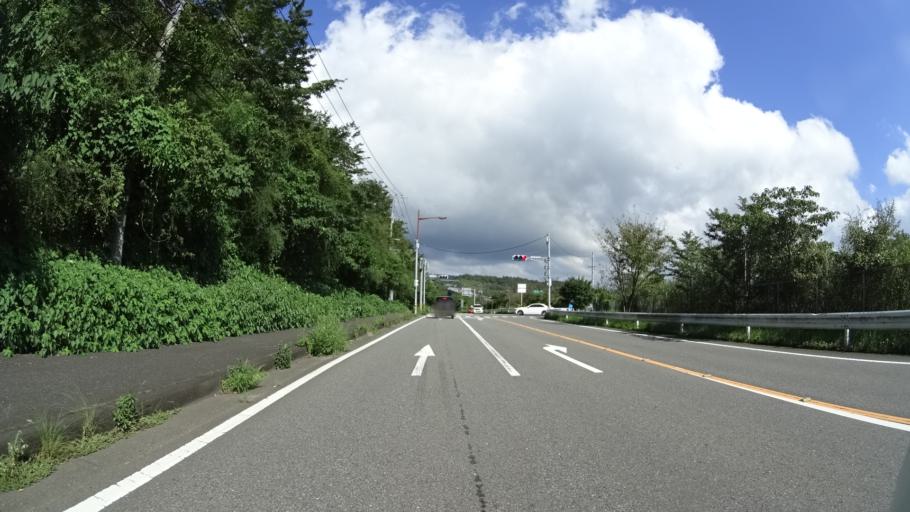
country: JP
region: Oita
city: Beppu
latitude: 33.3373
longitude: 131.4601
